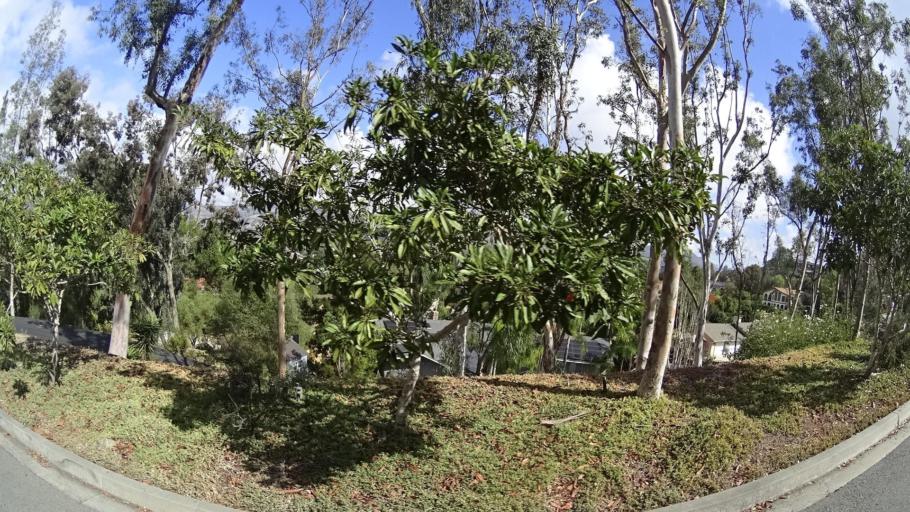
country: US
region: California
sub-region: San Diego County
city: Granite Hills
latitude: 32.7771
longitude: -116.9040
